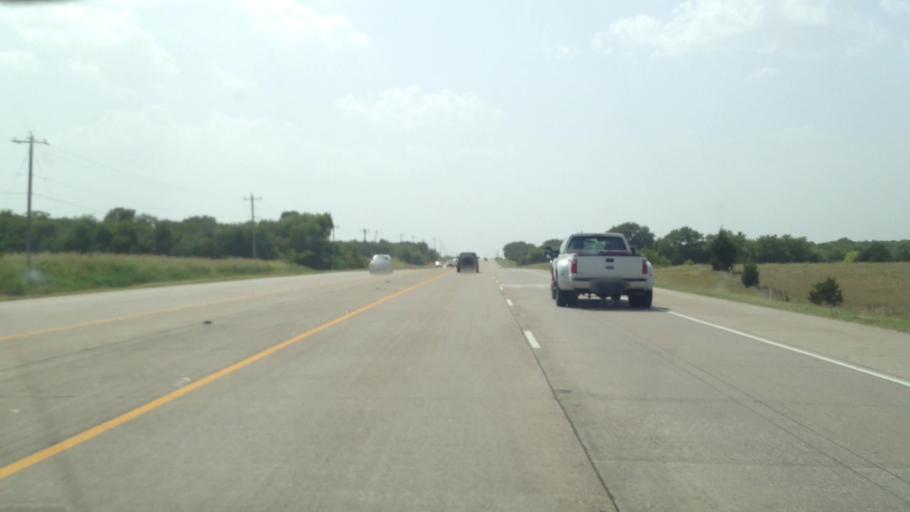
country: US
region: Texas
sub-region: Collin County
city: Princeton
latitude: 33.1700
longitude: -96.4722
